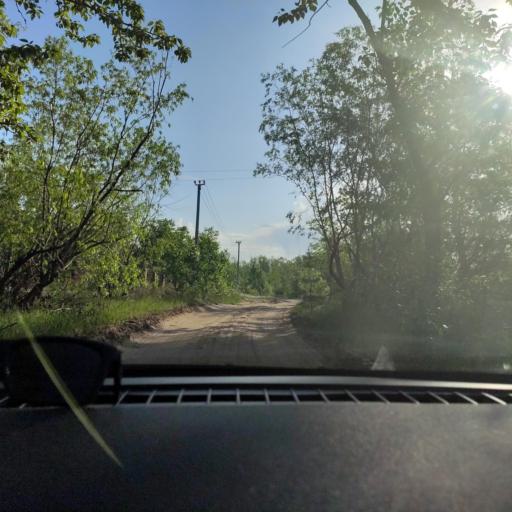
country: RU
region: Samara
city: Volzhskiy
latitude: 53.4336
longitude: 50.1636
